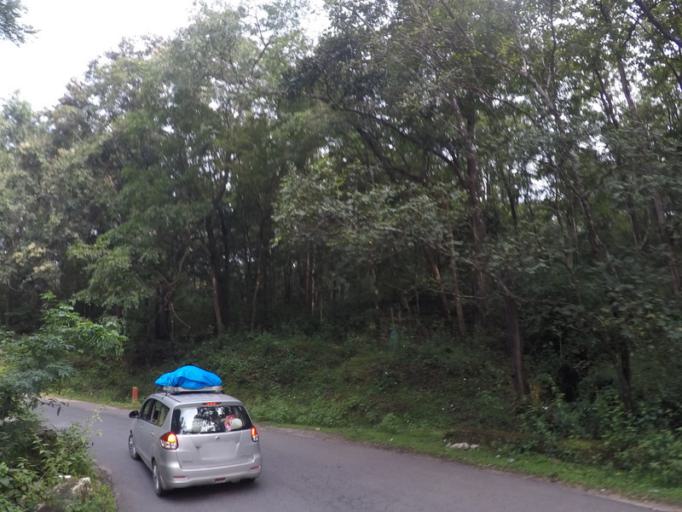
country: IN
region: Karnataka
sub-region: Chikmagalur
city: Koppa
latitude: 13.3547
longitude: 75.4948
